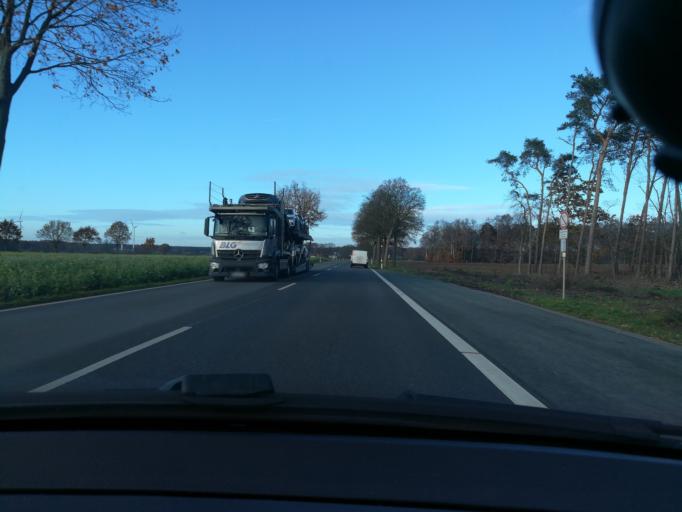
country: DE
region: Lower Saxony
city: Kirchdorf
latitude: 52.5539
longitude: 8.8595
